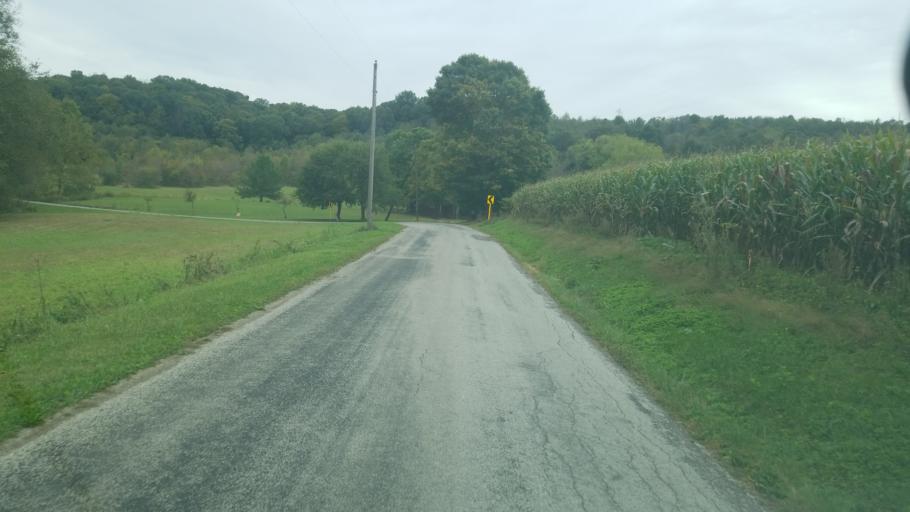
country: US
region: Ohio
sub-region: Sandusky County
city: Bellville
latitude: 40.5936
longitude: -82.4540
